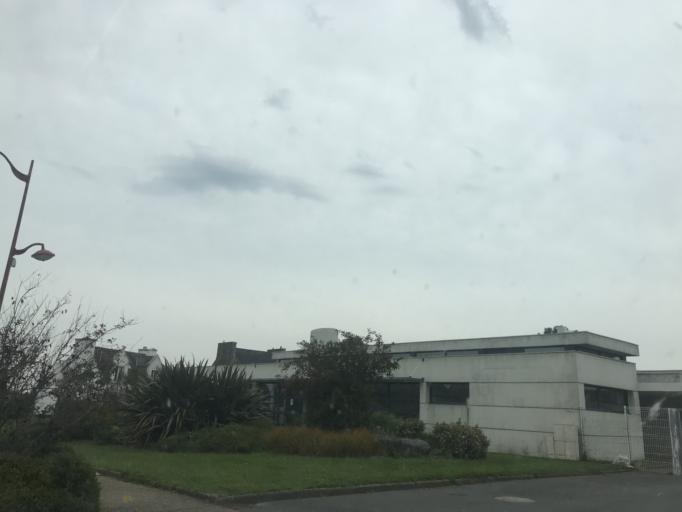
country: FR
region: Brittany
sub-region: Departement du Finistere
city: Plouneour-Menez
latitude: 48.4402
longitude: -3.8903
